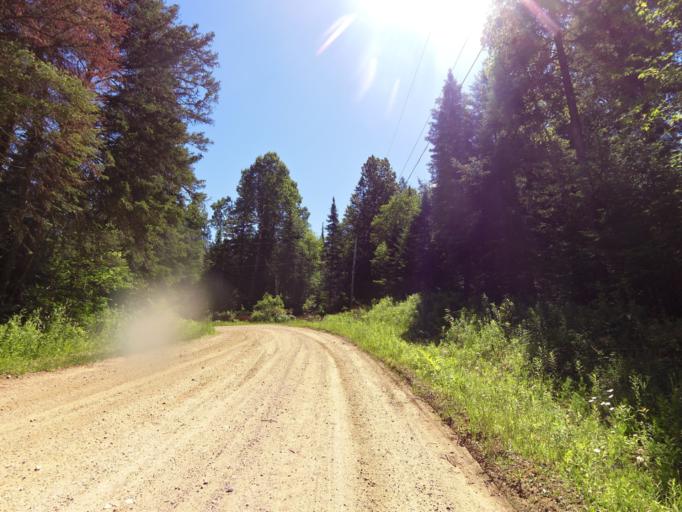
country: CA
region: Quebec
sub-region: Laurentides
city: Brownsburg-Chatham
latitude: 45.8278
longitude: -74.5058
